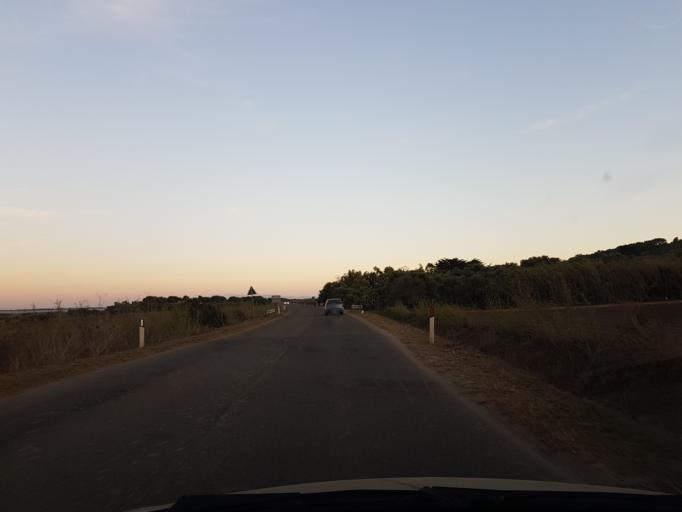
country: IT
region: Sardinia
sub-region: Provincia di Oristano
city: Cabras
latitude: 39.9584
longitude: 8.4537
